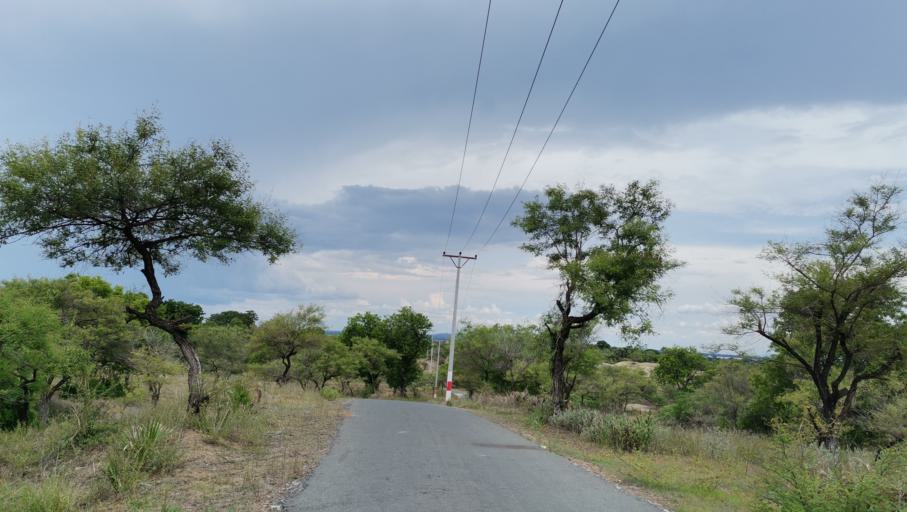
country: MM
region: Mandalay
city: Myingyan
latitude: 21.8233
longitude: 95.3953
